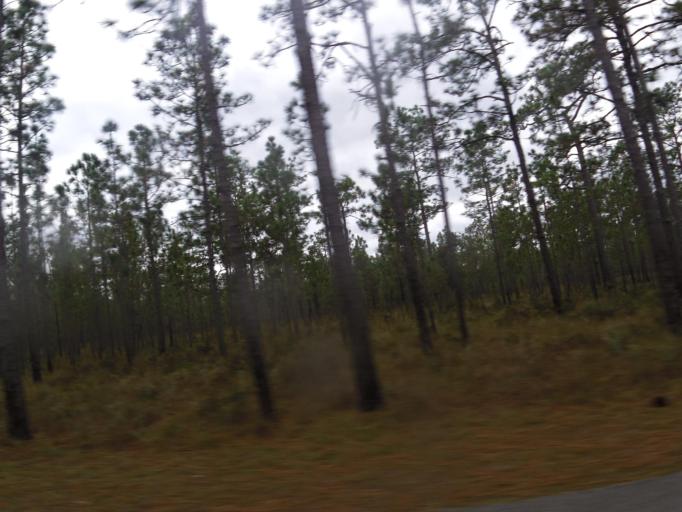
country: US
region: Florida
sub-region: Clay County
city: Keystone Heights
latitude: 29.8457
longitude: -81.9544
